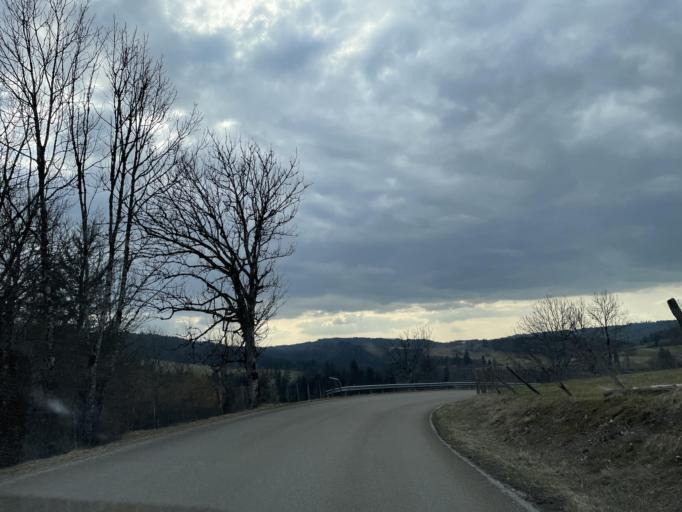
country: FR
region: Franche-Comte
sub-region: Departement du Doubs
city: Gilley
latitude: 47.0349
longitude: 6.5207
